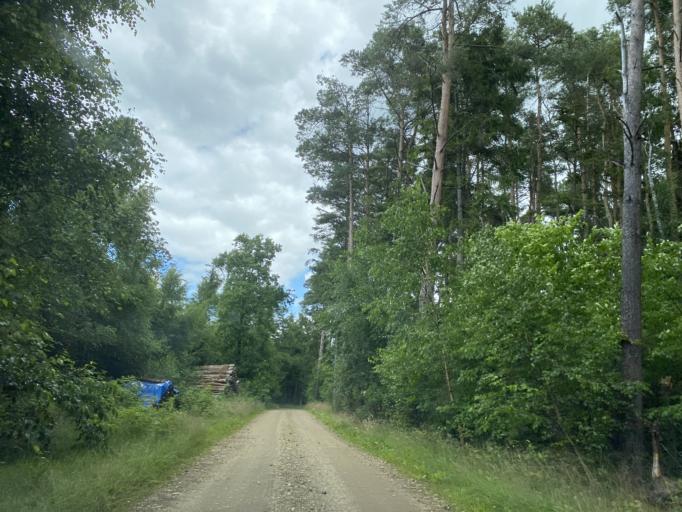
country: DK
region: Central Jutland
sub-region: Viborg Kommune
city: Bjerringbro
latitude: 56.2857
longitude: 9.6551
